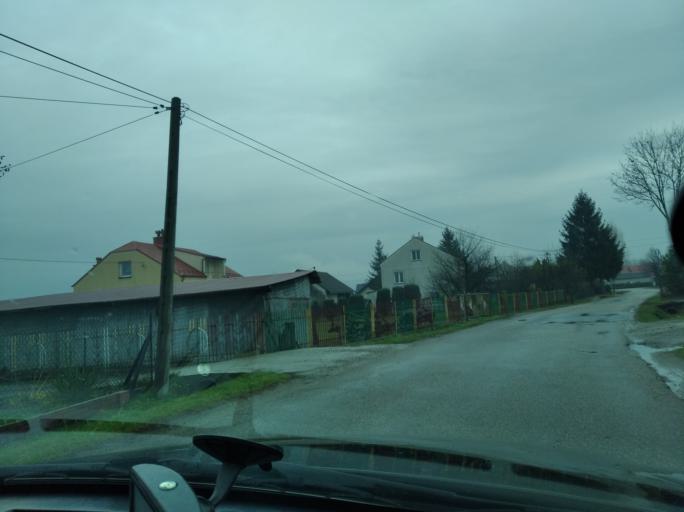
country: PL
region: Subcarpathian Voivodeship
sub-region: Powiat strzyzowski
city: Czudec
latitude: 49.9298
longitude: 21.8505
